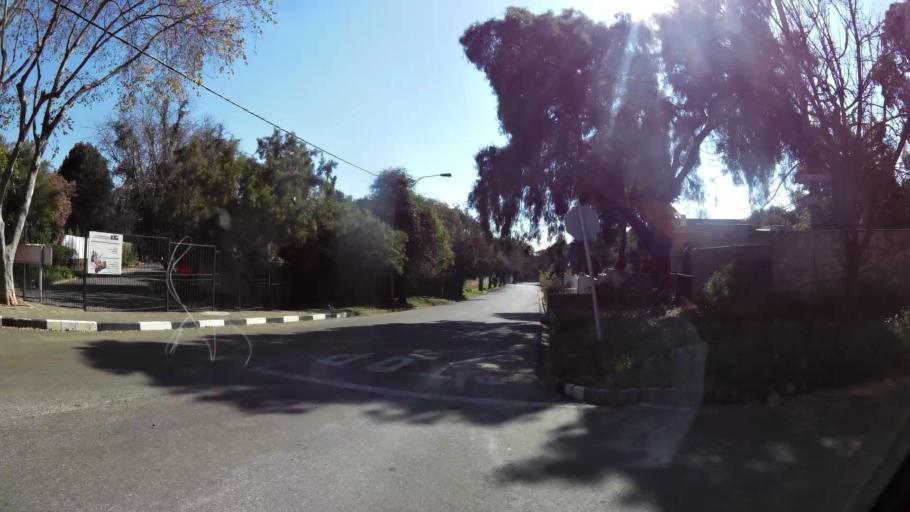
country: ZA
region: Gauteng
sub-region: City of Johannesburg Metropolitan Municipality
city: Johannesburg
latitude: -26.1740
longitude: 28.0357
